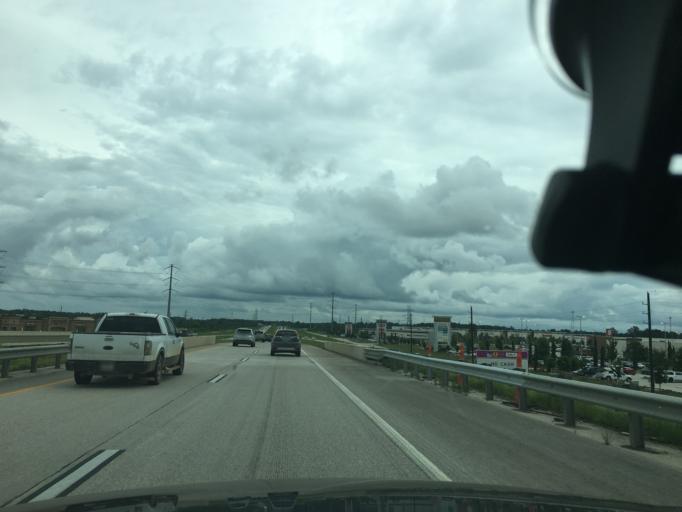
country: US
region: Texas
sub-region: Montgomery County
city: The Woodlands
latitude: 30.0875
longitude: -95.5259
